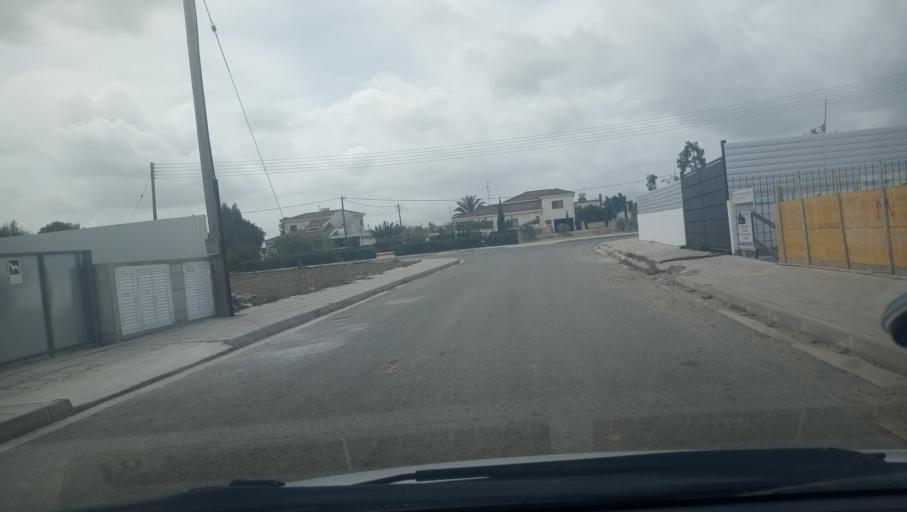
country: CY
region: Lefkosia
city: Pano Deftera
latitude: 35.0739
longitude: 33.2687
